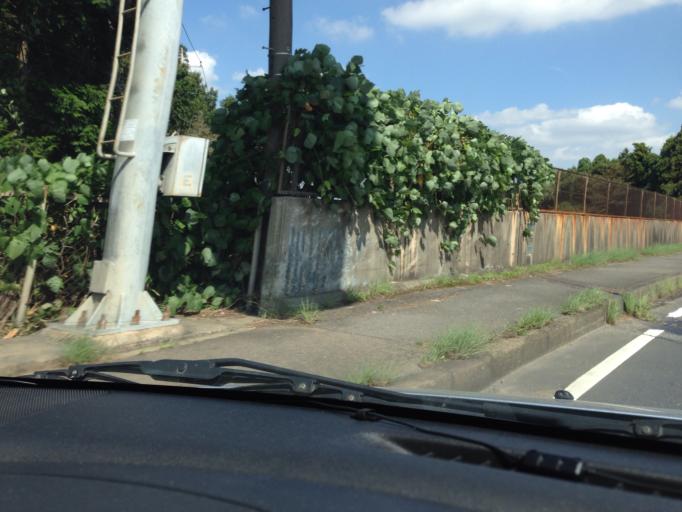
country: JP
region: Ibaraki
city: Naka
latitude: 36.0594
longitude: 140.1561
